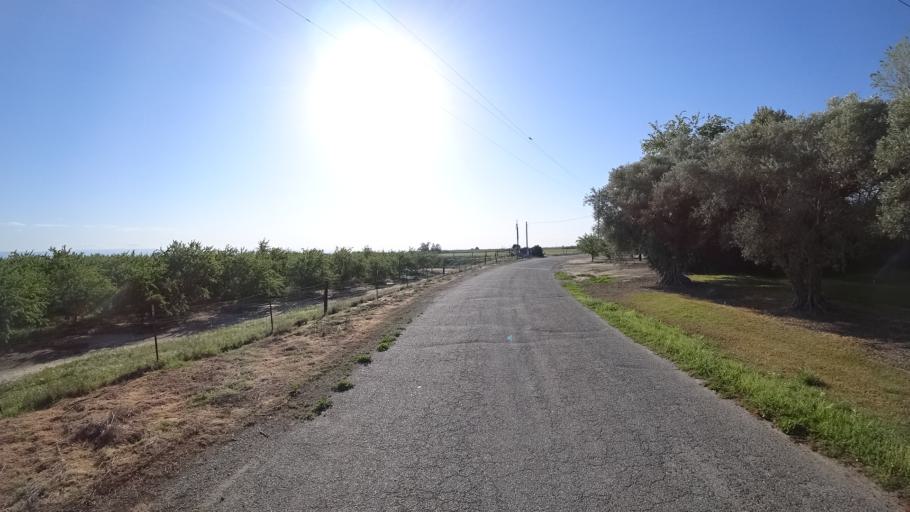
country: US
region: California
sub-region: Glenn County
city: Orland
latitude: 39.7179
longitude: -122.1682
